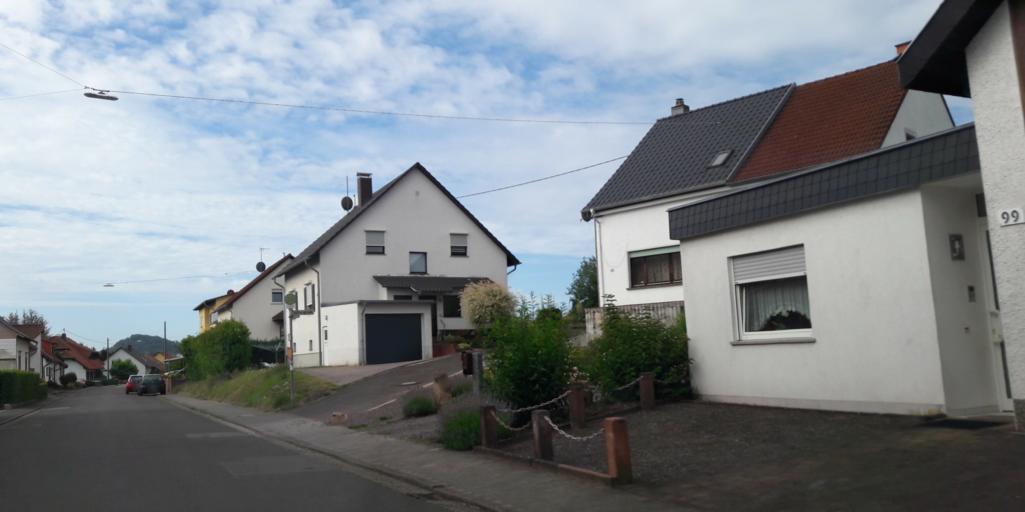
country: DE
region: Saarland
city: Puttlingen
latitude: 49.3130
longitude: 6.9014
